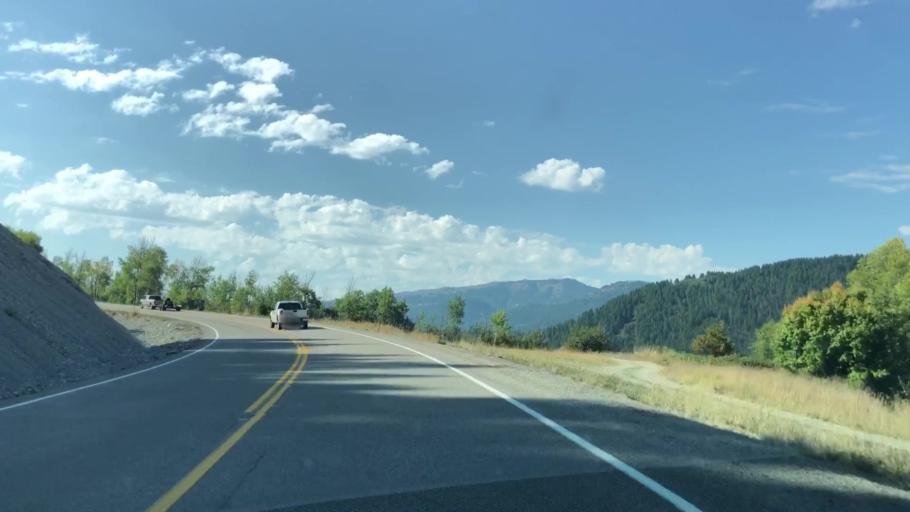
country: US
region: Idaho
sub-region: Teton County
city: Victor
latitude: 43.3150
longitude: -111.1464
